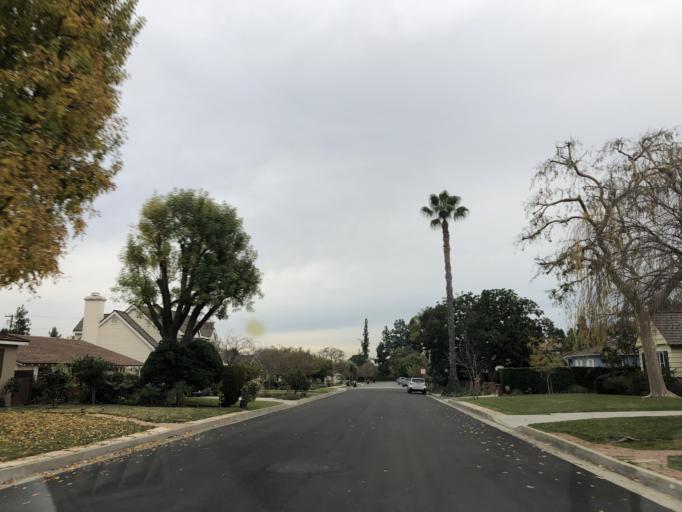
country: US
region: California
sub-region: Los Angeles County
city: San Marino
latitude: 34.1162
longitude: -118.0962
